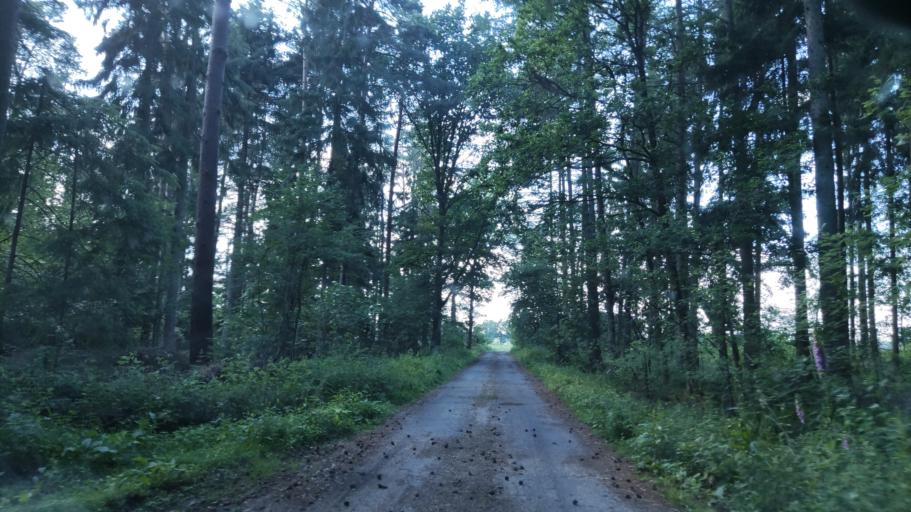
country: DE
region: Lower Saxony
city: Hanstedt Eins
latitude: 53.0819
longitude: 10.4111
